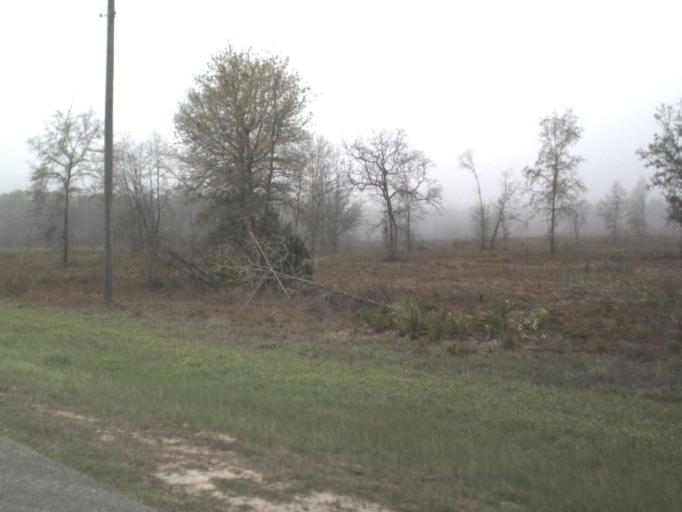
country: US
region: Florida
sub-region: Gadsden County
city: Gretna
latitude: 30.5052
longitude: -84.7129
